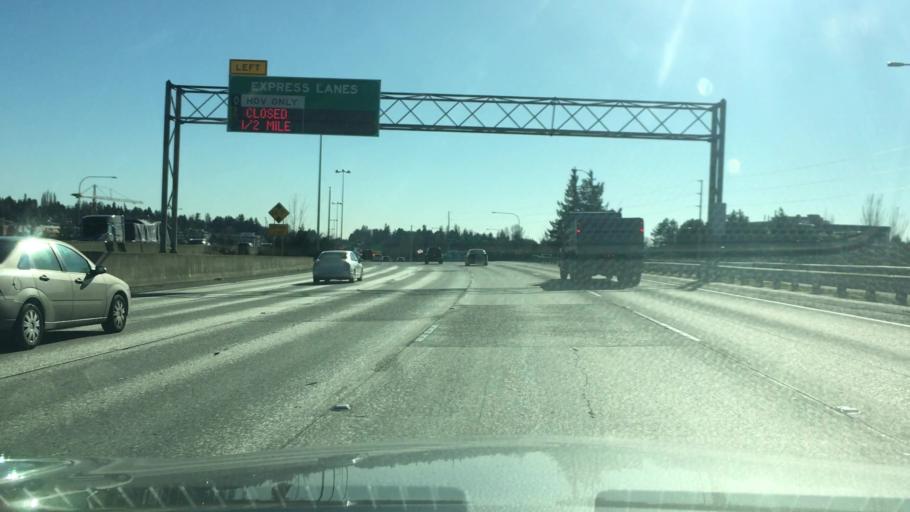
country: US
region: Washington
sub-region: King County
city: Shoreline
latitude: 47.7098
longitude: -122.3300
